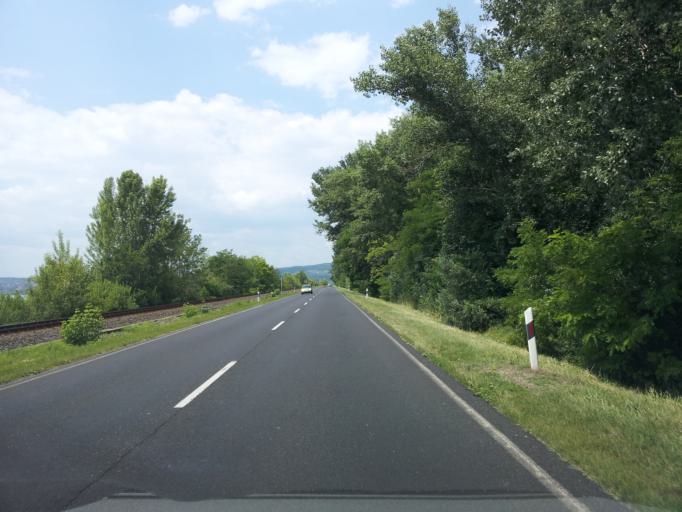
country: HU
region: Veszprem
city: Balatonkenese
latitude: 47.0402
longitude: 18.0703
